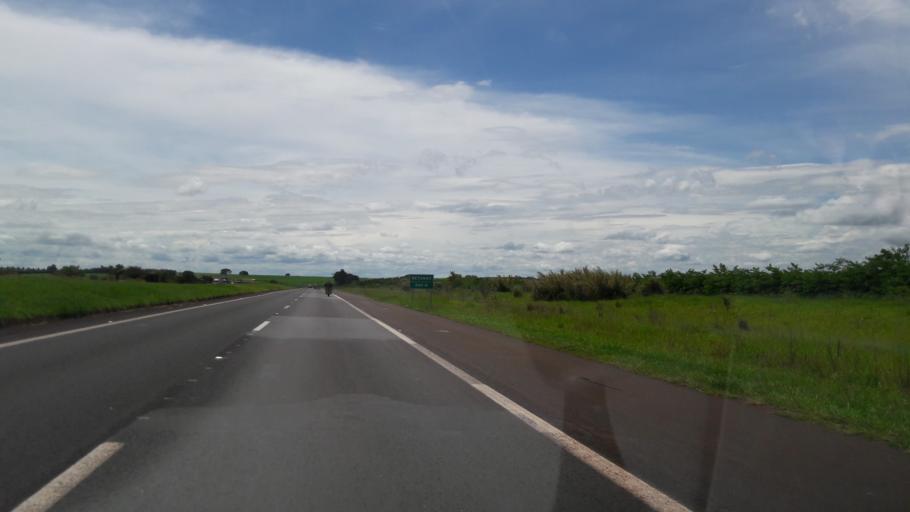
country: BR
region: Sao Paulo
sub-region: Avare
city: Avare
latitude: -22.9433
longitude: -48.9011
